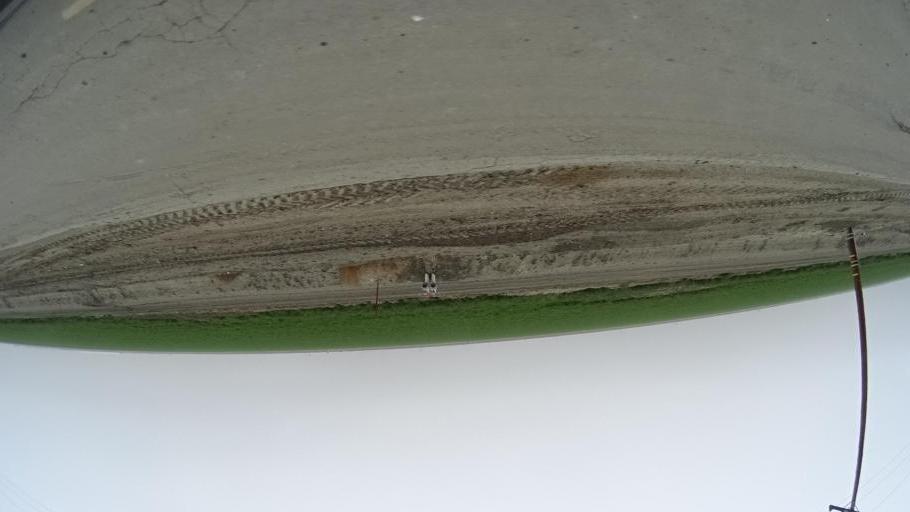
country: US
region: California
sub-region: Kern County
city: Rosedale
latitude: 35.1944
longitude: -119.2127
